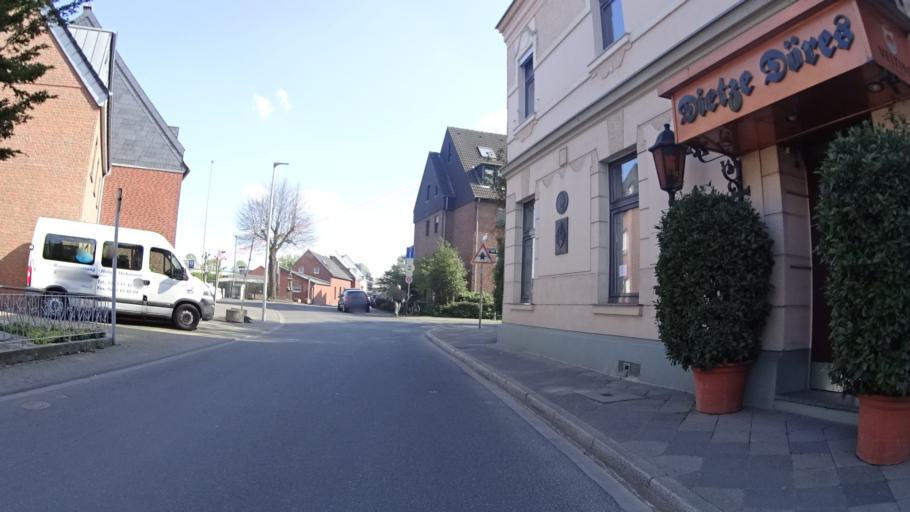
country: DE
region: North Rhine-Westphalia
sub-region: Regierungsbezirk Dusseldorf
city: Dusseldorf
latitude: 51.1883
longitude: 6.7719
